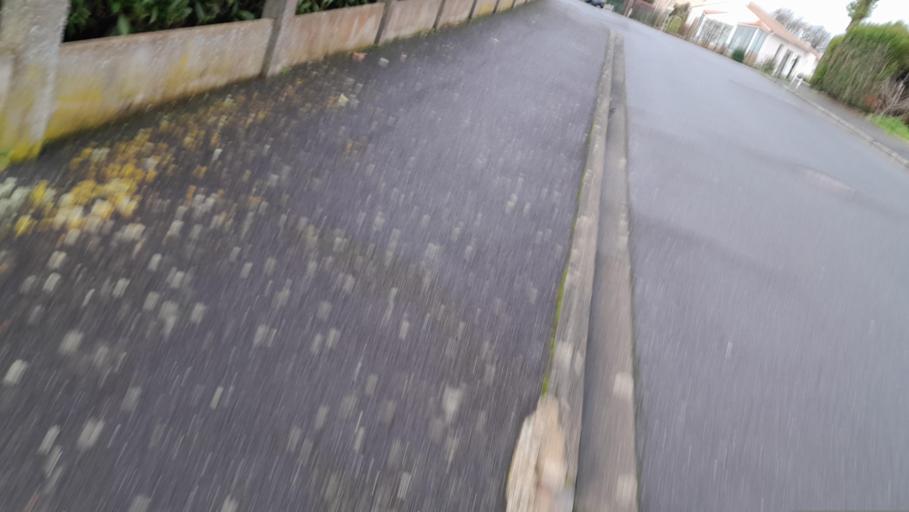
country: FR
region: Pays de la Loire
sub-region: Departement de la Loire-Atlantique
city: Oudon
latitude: 47.3501
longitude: -1.2795
